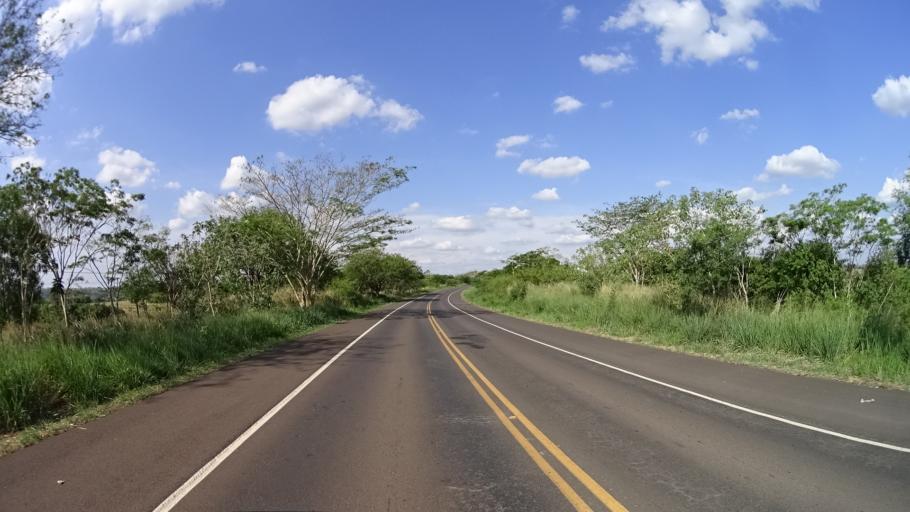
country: BR
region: Sao Paulo
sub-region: Urupes
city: Urupes
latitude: -21.0101
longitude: -49.2251
